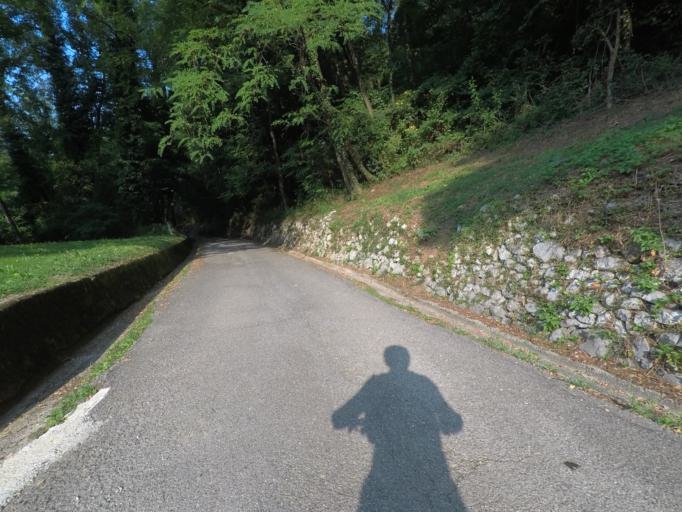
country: IT
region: Friuli Venezia Giulia
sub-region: Provincia di Pordenone
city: Travesio
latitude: 46.2032
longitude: 12.8714
